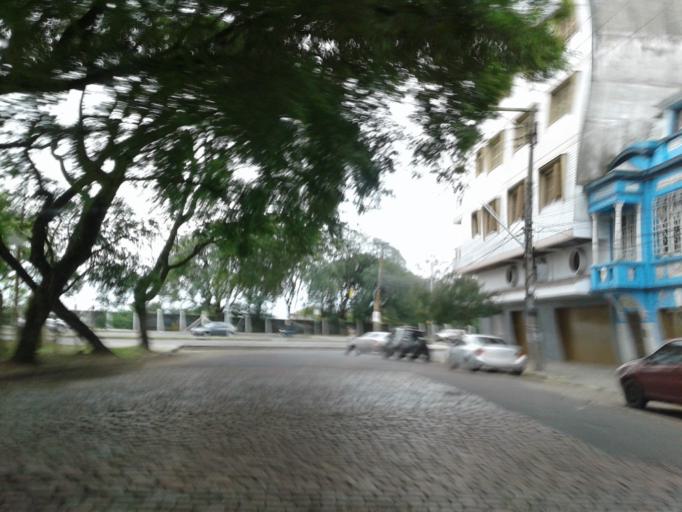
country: BR
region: Rio Grande do Sul
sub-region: Porto Alegre
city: Porto Alegre
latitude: -30.0340
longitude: -51.2397
